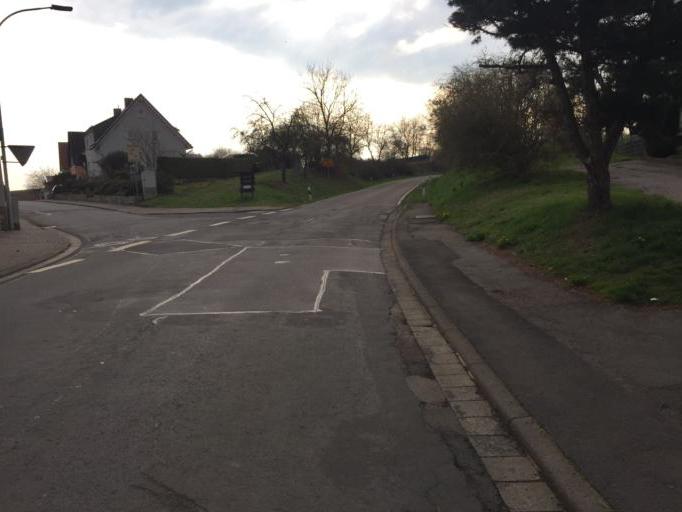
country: DE
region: Hesse
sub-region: Regierungsbezirk Giessen
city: Grunberg
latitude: 50.5688
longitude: 8.9623
